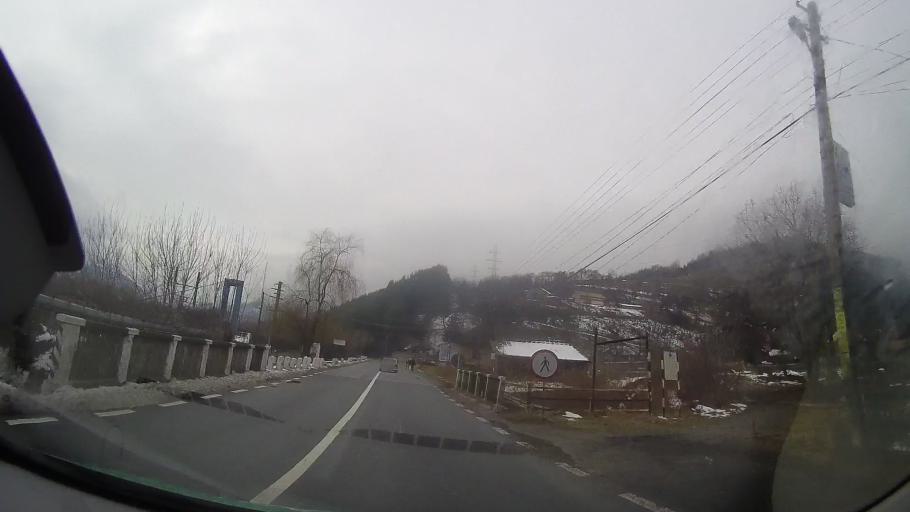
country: RO
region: Neamt
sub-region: Comuna Tasca
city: Tasca
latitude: 46.8797
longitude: 25.9825
